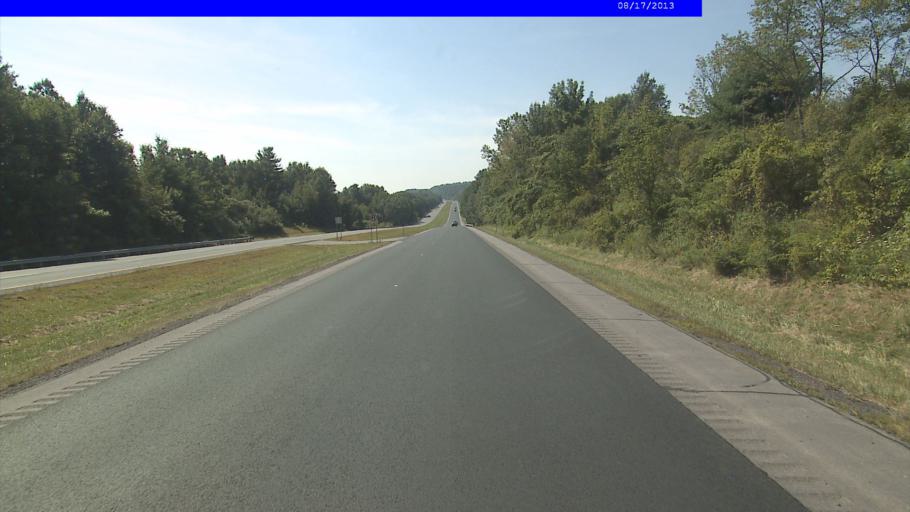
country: US
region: Vermont
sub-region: Windham County
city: Bellows Falls
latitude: 43.0613
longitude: -72.4704
